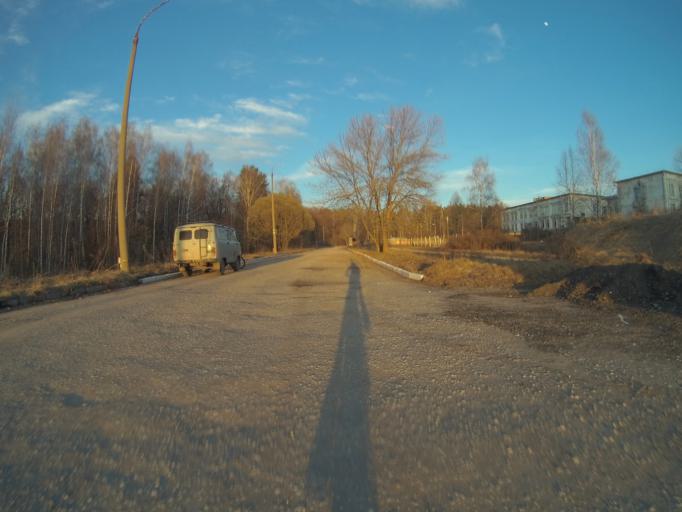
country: RU
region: Vladimir
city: Kommunar
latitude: 56.0632
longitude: 40.4907
